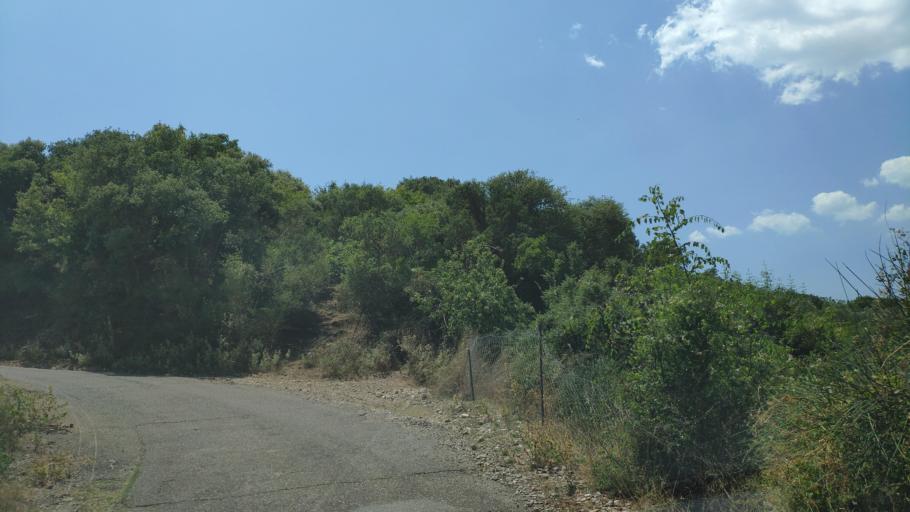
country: GR
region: West Greece
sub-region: Nomos Aitolias kai Akarnanias
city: Fitiai
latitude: 38.7128
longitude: 21.1753
